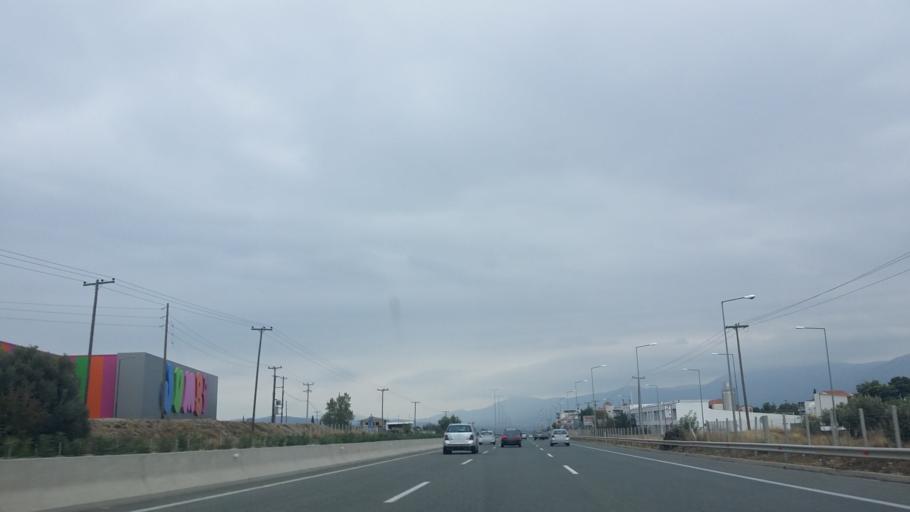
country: GR
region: Central Greece
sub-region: Nomos Voiotias
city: Oinofyta
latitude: 38.3149
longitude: 23.6320
